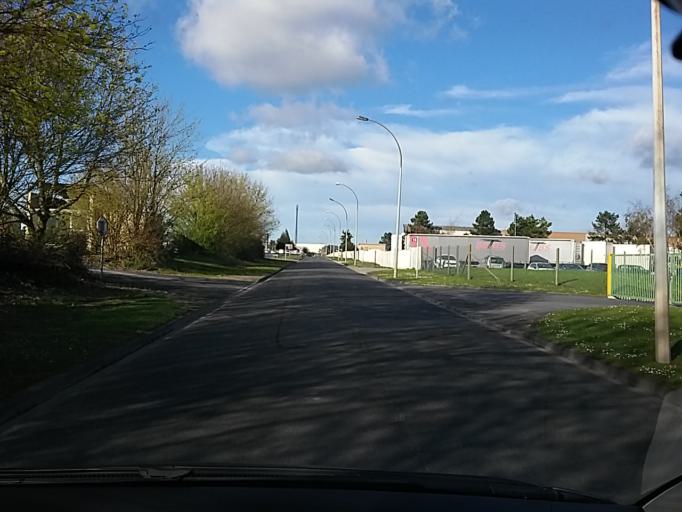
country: FR
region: Picardie
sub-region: Departement de la Somme
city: Dreuil-les-Amiens
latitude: 49.9305
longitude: 2.2640
